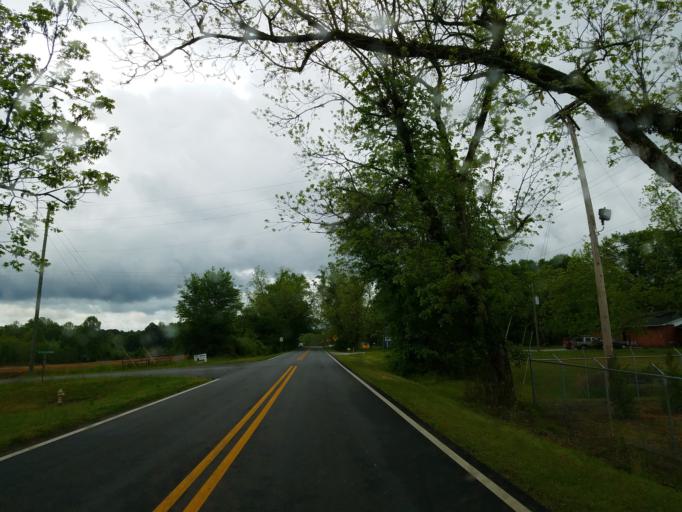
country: US
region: Georgia
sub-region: Lamar County
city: Barnesville
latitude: 33.1048
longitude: -84.1883
